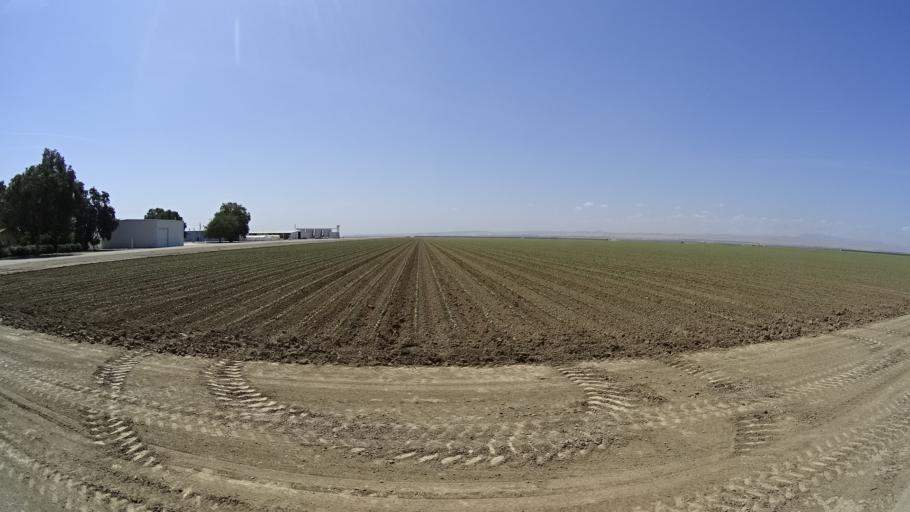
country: US
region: California
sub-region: Kings County
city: Kettleman City
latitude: 36.1378
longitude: -119.9865
